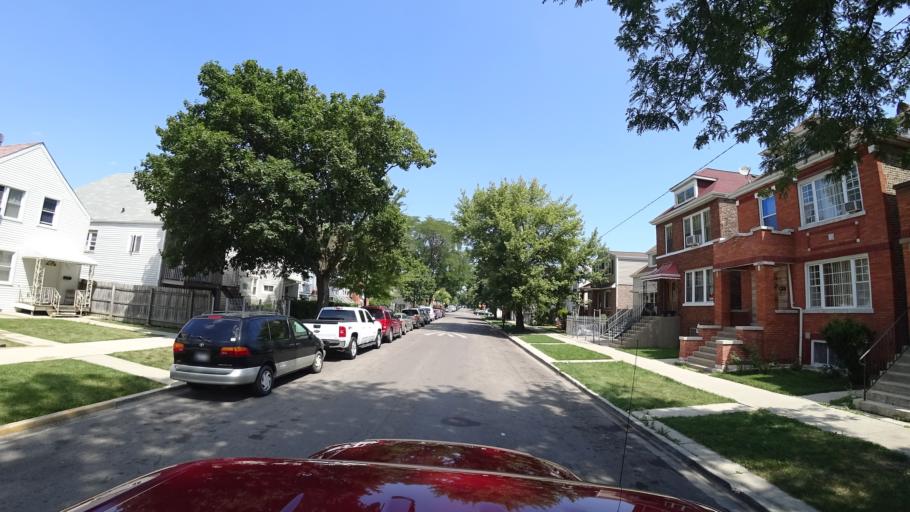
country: US
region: Illinois
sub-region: Cook County
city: Chicago
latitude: 41.8093
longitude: -87.6930
